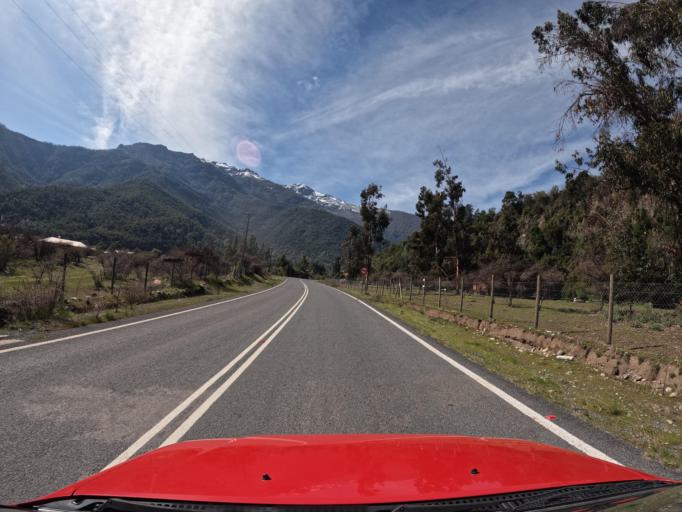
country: CL
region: Maule
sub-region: Provincia de Curico
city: Teno
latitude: -35.0015
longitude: -70.8239
